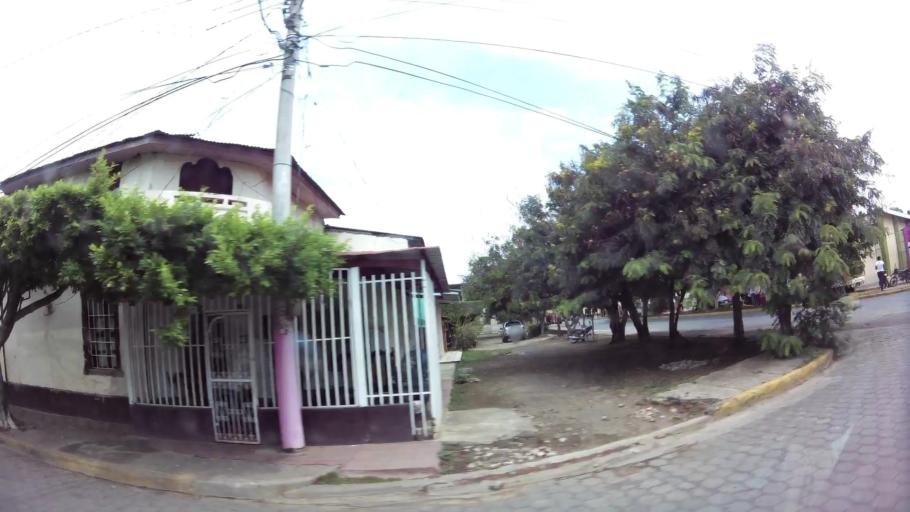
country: NI
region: Rivas
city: Rivas
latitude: 11.4420
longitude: -85.8269
